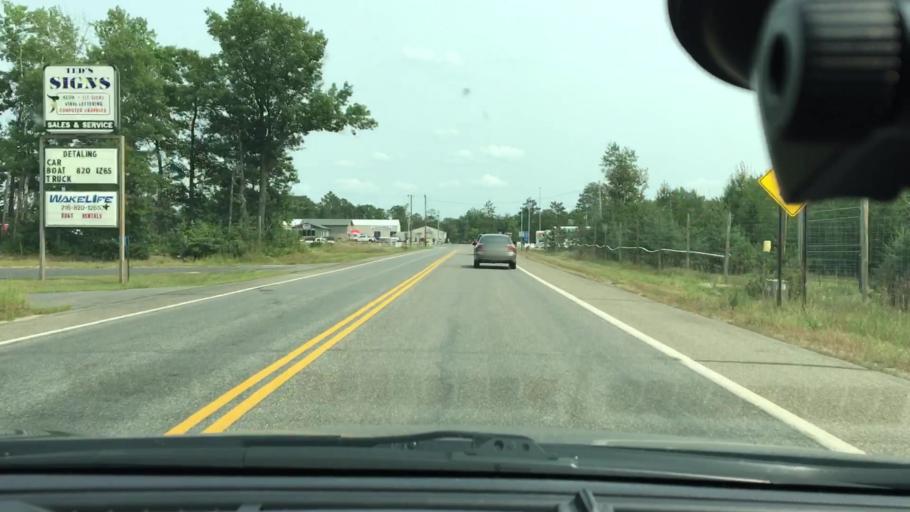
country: US
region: Minnesota
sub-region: Cass County
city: East Gull Lake
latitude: 46.4128
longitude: -94.2886
